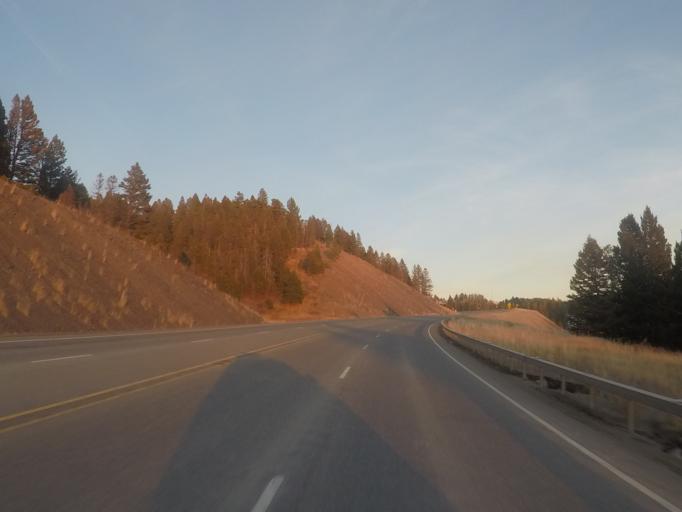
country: US
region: Montana
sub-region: Lewis and Clark County
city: Helena West Side
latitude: 46.5594
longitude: -112.3468
